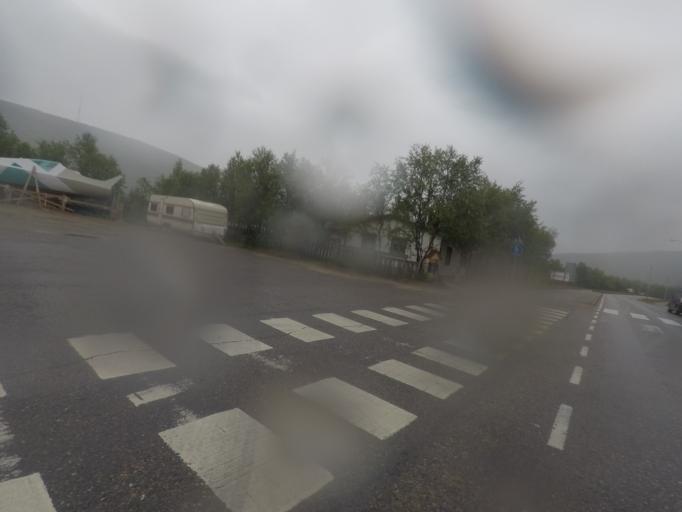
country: FI
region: Lapland
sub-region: Pohjois-Lappi
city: Utsjoki
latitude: 69.9068
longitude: 27.0252
